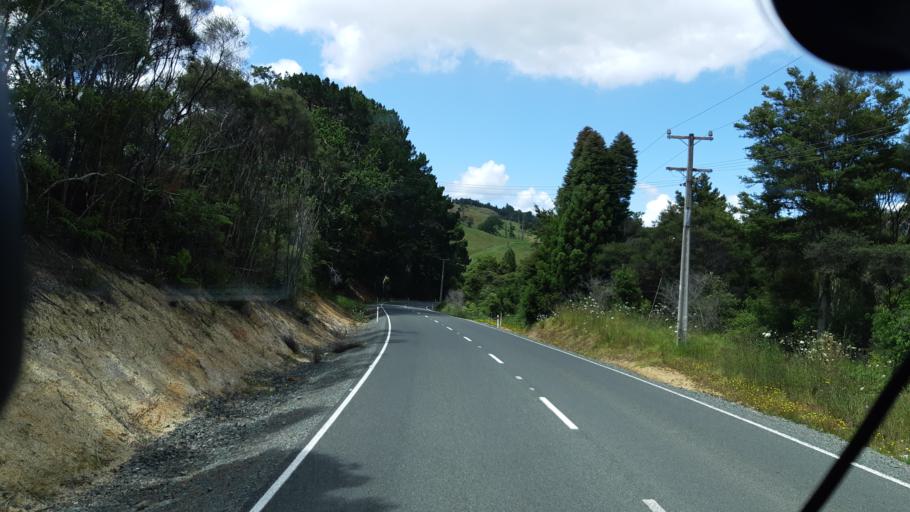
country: NZ
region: Northland
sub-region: Far North District
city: Taipa
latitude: -35.2385
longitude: 173.5420
